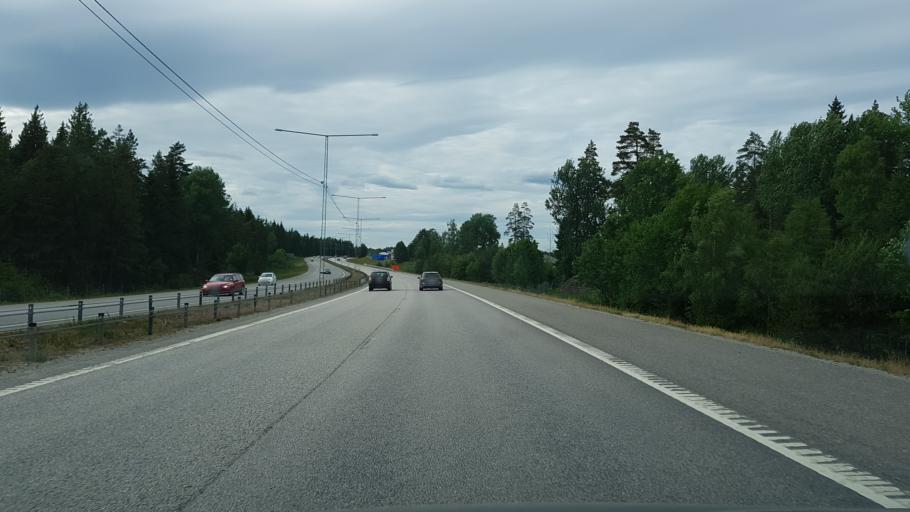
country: SE
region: Stockholm
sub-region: Haninge Kommun
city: Haninge
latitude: 59.1439
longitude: 18.1608
